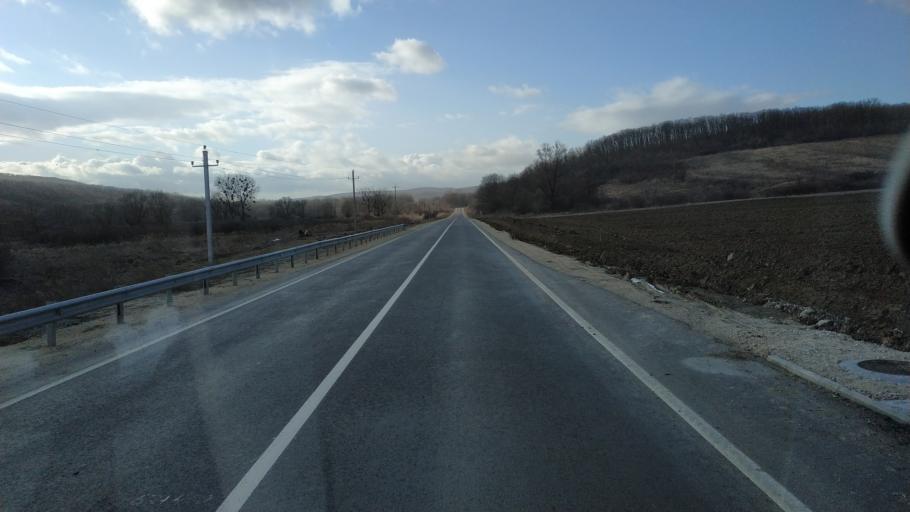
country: MD
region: Calarasi
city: Calarasi
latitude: 47.3004
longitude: 28.1508
